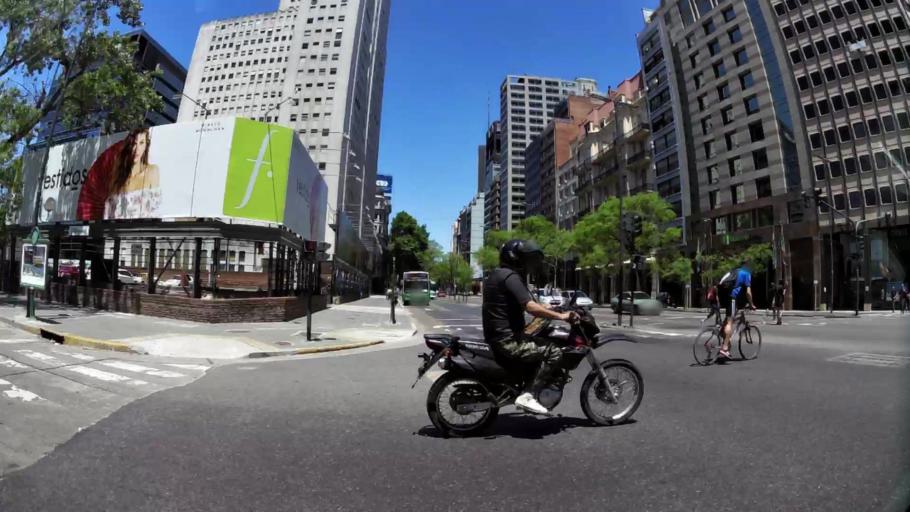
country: AR
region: Buenos Aires F.D.
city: Buenos Aires
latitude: -34.5984
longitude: -58.3710
